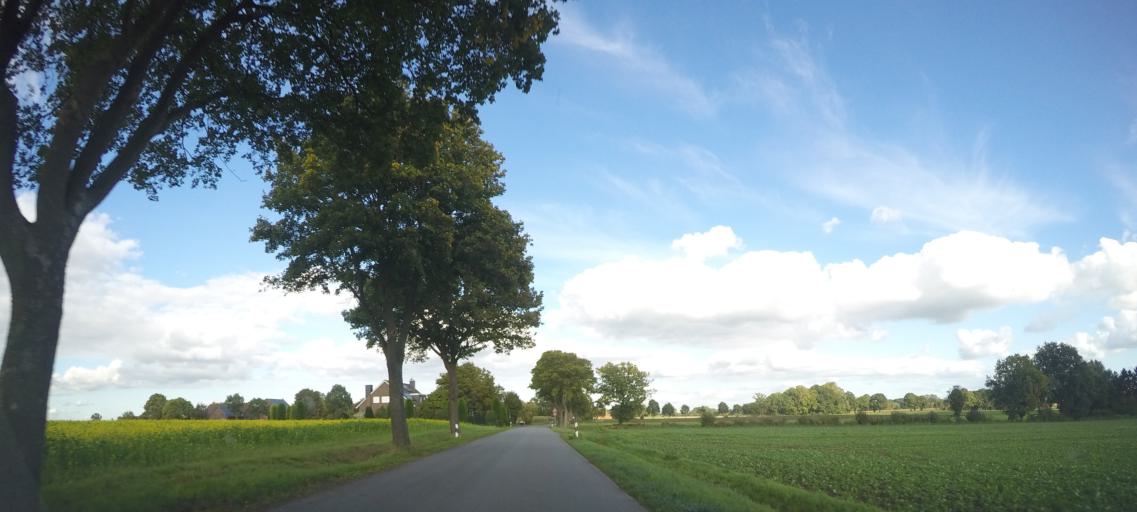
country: DE
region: North Rhine-Westphalia
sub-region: Regierungsbezirk Munster
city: Wadersloh
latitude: 51.6876
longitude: 8.1859
